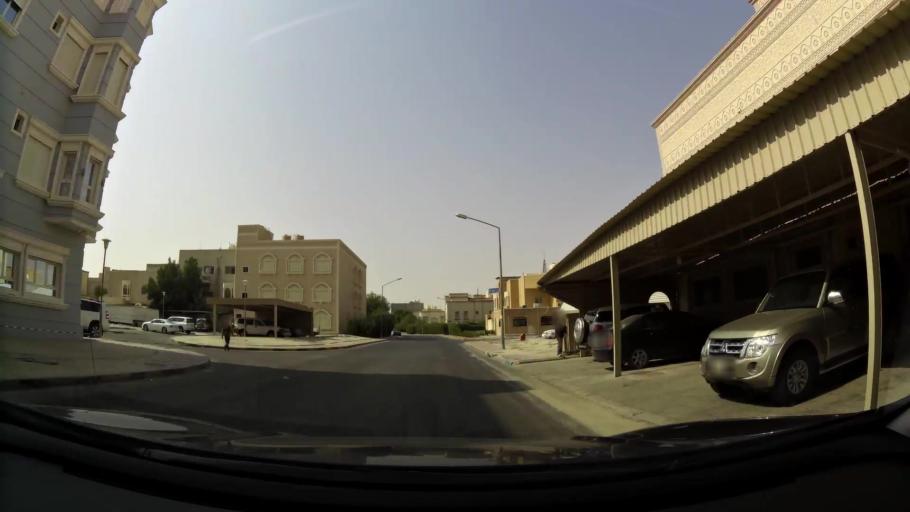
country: KW
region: Muhafazat al Jahra'
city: Al Jahra'
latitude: 29.3245
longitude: 47.6675
